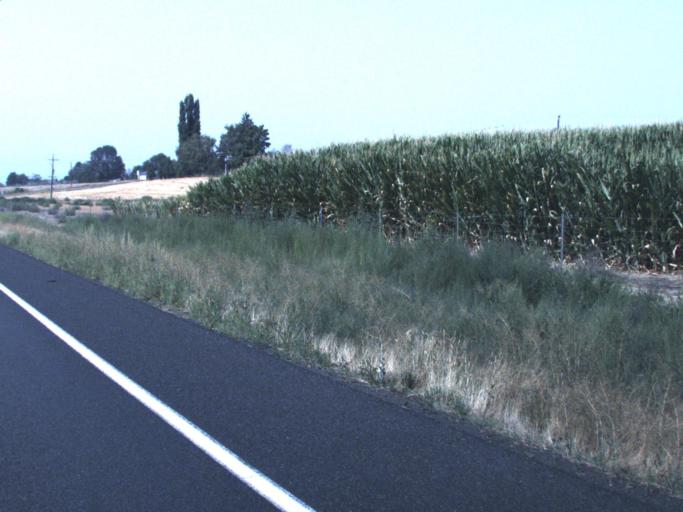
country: US
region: Washington
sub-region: Yakima County
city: Zillah
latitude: 46.5338
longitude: -120.2878
